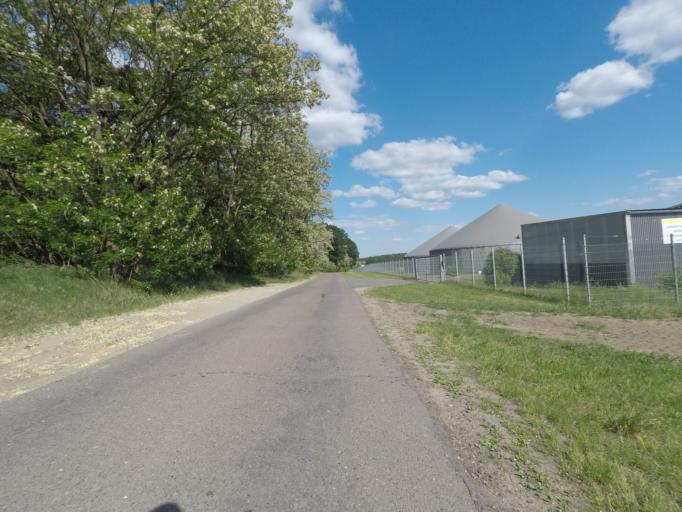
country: DE
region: Brandenburg
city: Britz
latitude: 52.8695
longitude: 13.7675
